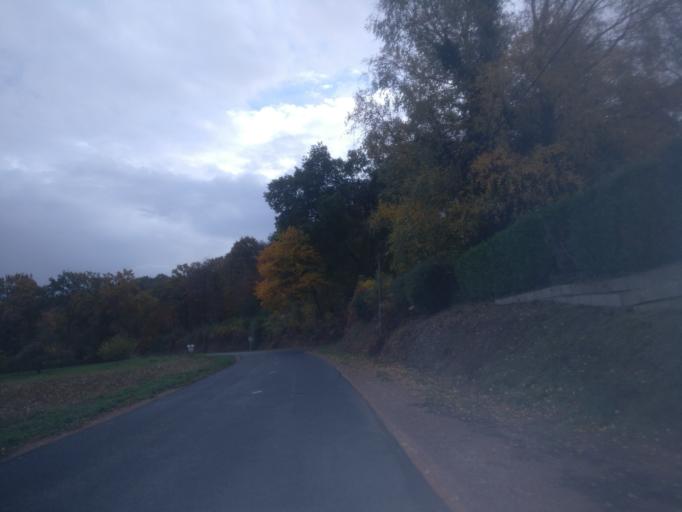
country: FR
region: Brittany
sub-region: Departement d'Ille-et-Vilaine
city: Guichen
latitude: 48.0045
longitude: -1.7921
